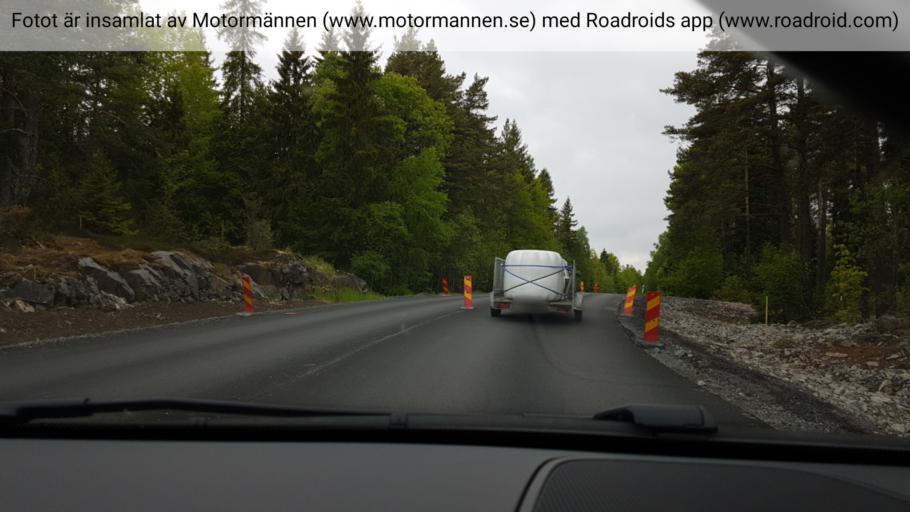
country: SE
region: Uppsala
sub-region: Osthammars Kommun
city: Gimo
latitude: 60.1242
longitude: 18.1494
